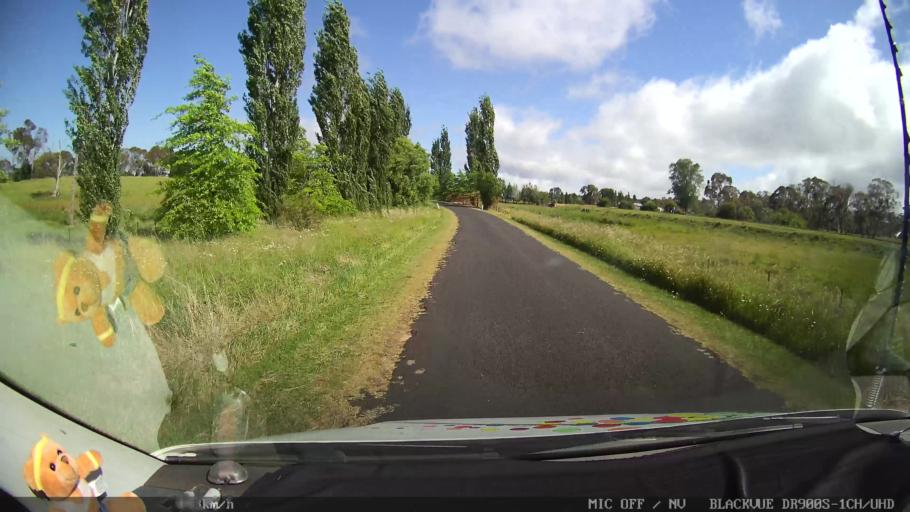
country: AU
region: New South Wales
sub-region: Guyra
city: Guyra
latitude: -30.0249
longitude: 151.6609
